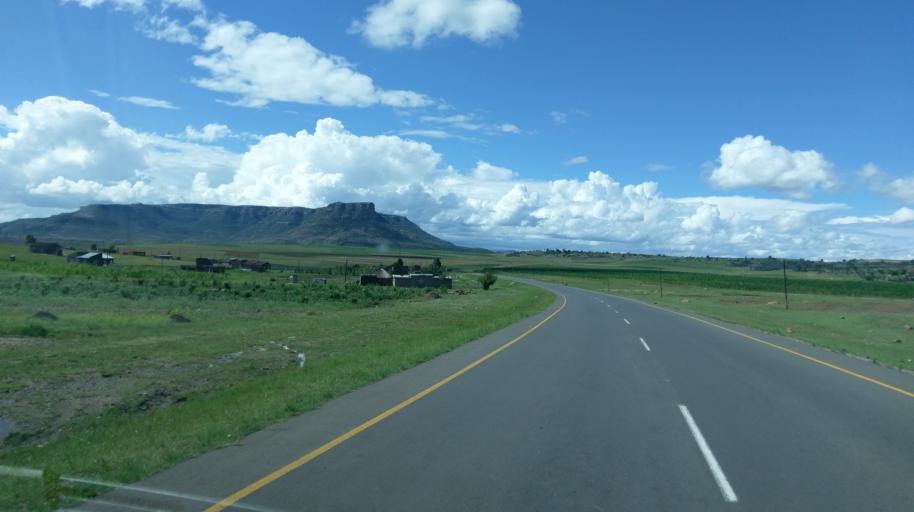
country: LS
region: Mafeteng
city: Mafeteng
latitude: -29.6667
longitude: 27.4534
